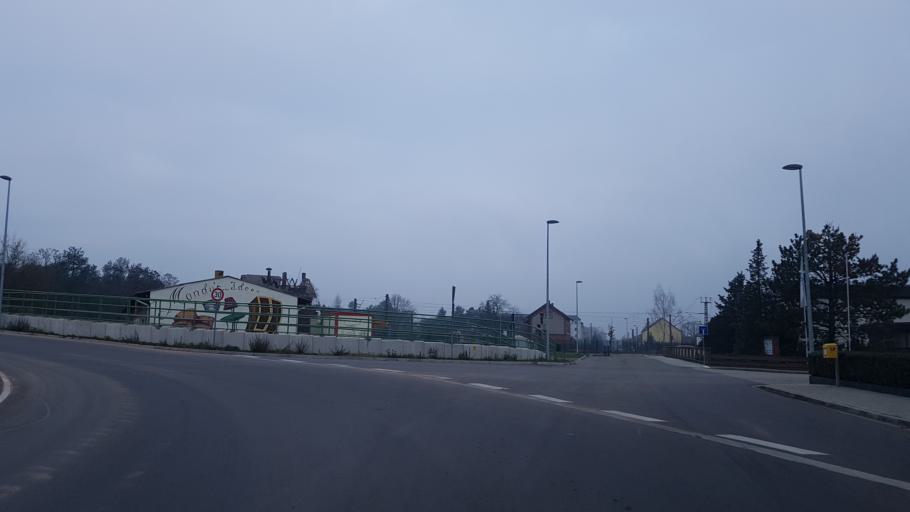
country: DE
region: Brandenburg
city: Ruckersdorf
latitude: 51.5673
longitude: 13.5757
